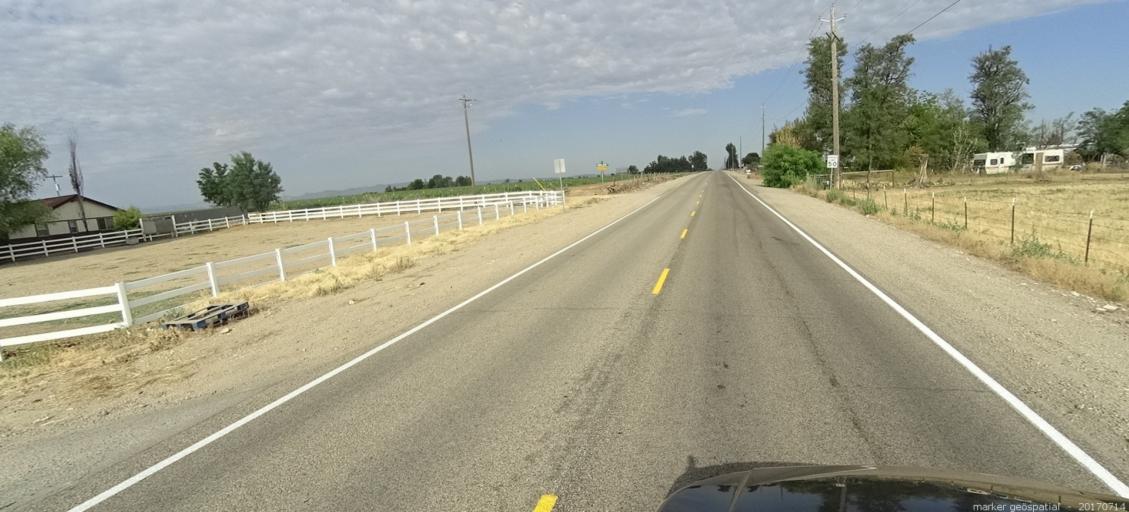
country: US
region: Idaho
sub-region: Ada County
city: Kuna
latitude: 43.4884
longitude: -116.4379
